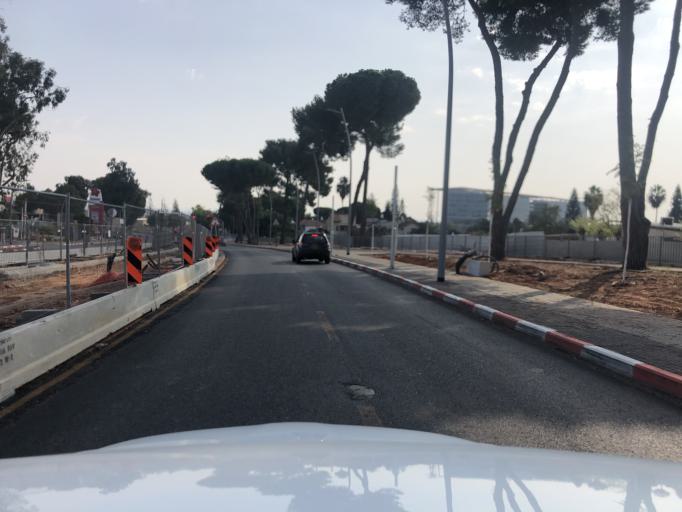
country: IL
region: Central District
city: Kfar Saba
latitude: 32.1709
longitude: 34.9248
